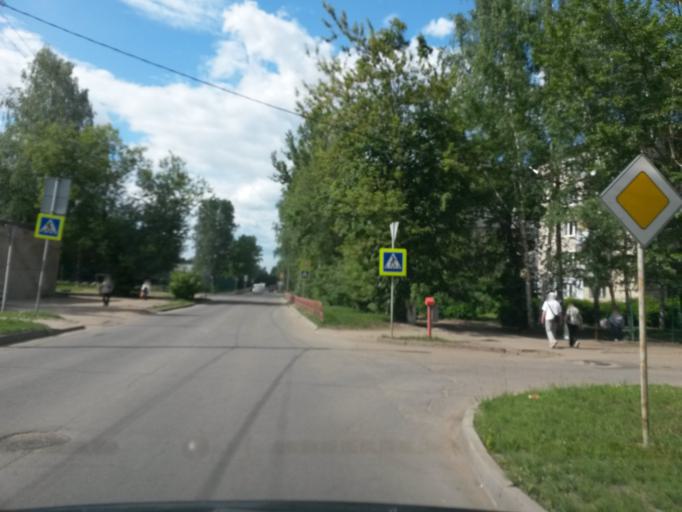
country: RU
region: Jaroslavl
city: Yaroslavl
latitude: 57.6478
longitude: 39.9392
